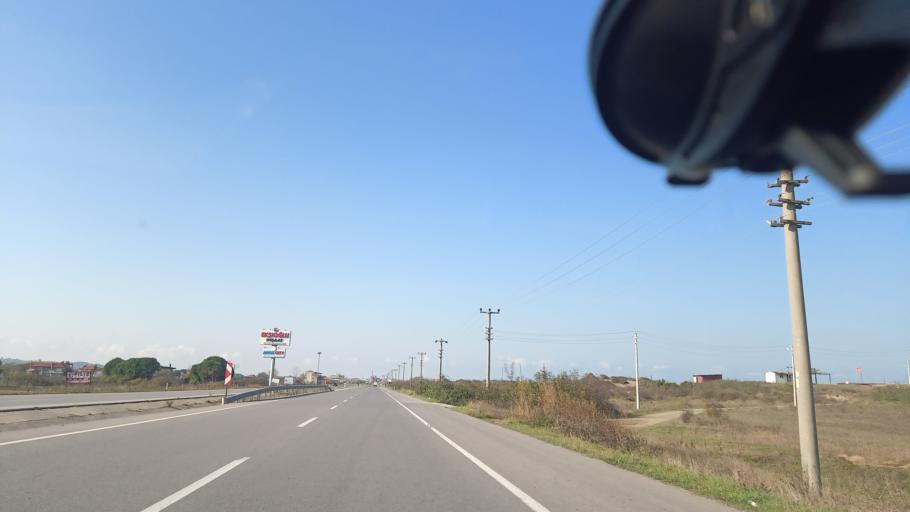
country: TR
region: Sakarya
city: Karasu
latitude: 41.0838
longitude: 30.7594
